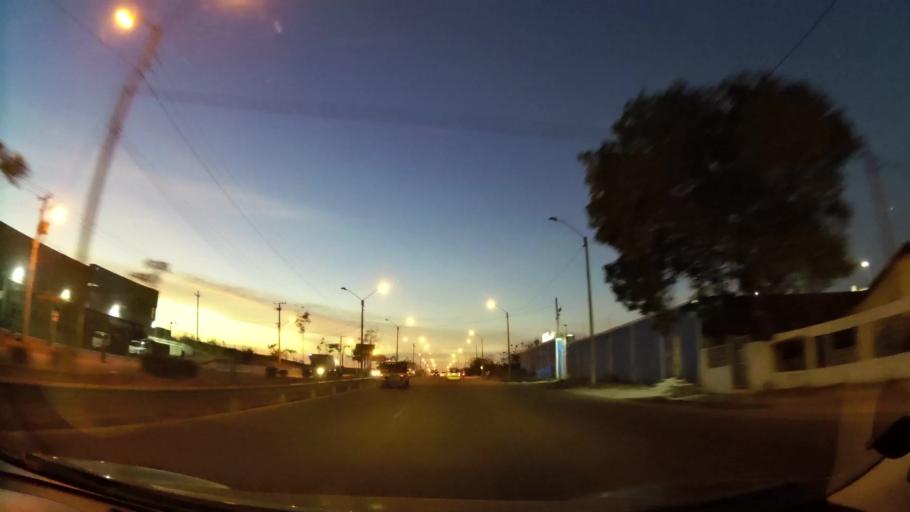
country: CO
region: Atlantico
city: Barranquilla
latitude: 10.9278
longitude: -74.8270
